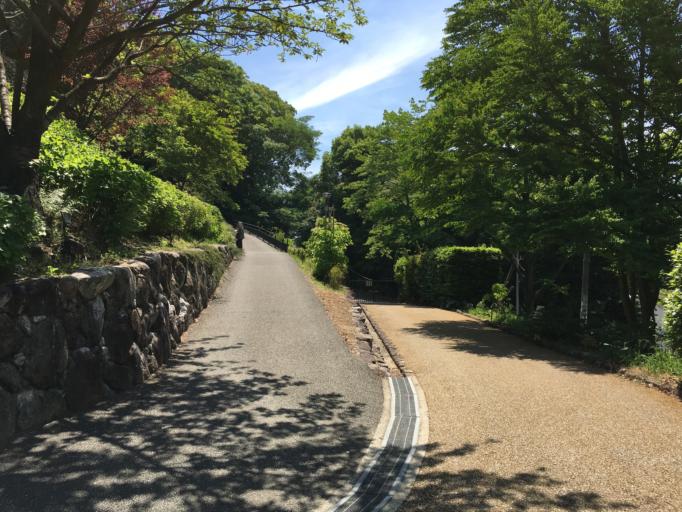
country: JP
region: Fukuoka
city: Fukuoka-shi
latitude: 33.5698
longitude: 130.3911
